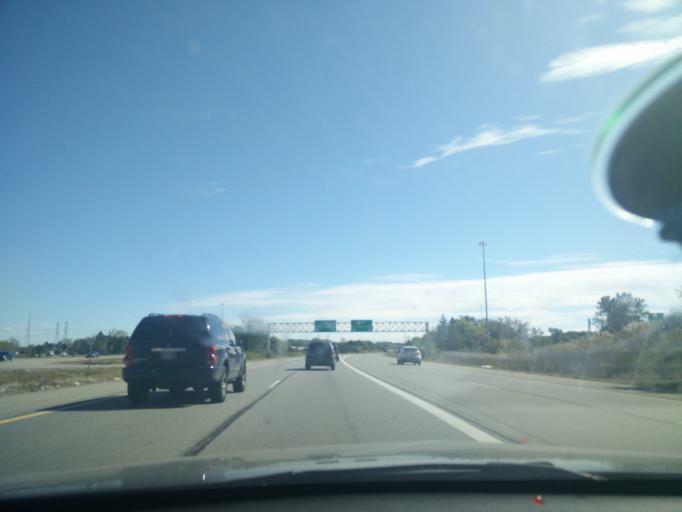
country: US
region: Michigan
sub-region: Oakland County
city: Novi
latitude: 42.4843
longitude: -83.4476
